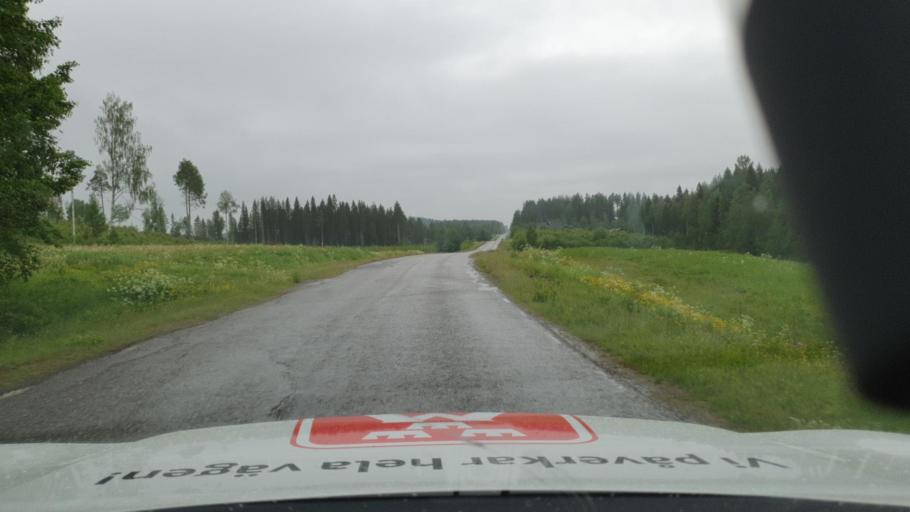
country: SE
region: Vaesterbotten
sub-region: Nordmalings Kommun
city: Nordmaling
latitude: 63.8088
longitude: 19.5018
